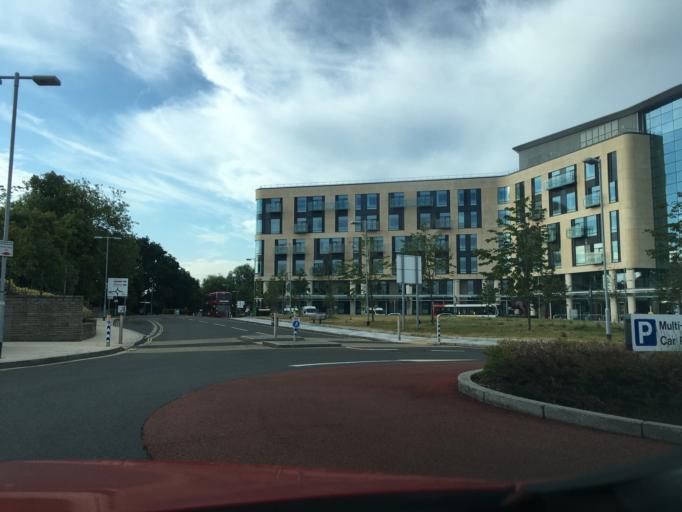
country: GB
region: England
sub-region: Bristol
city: Bristol
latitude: 51.4974
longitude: -2.5919
